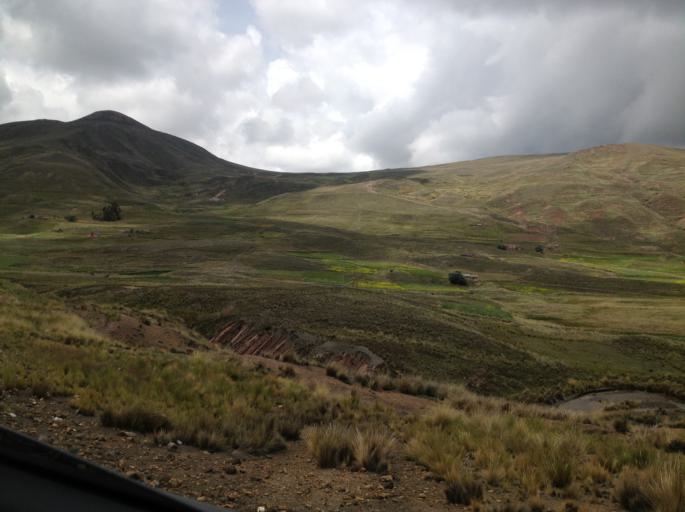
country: BO
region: La Paz
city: Yumani
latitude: -15.7682
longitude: -68.9760
